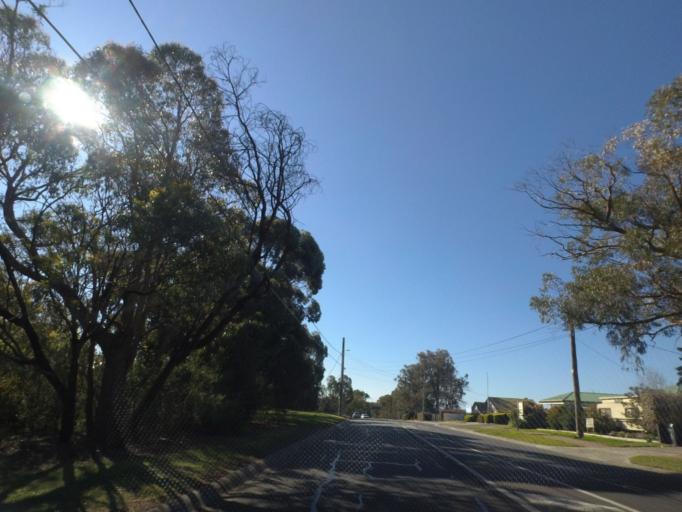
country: AU
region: Victoria
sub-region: Maroondah
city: Croydon Hills
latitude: -37.7719
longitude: 145.2759
